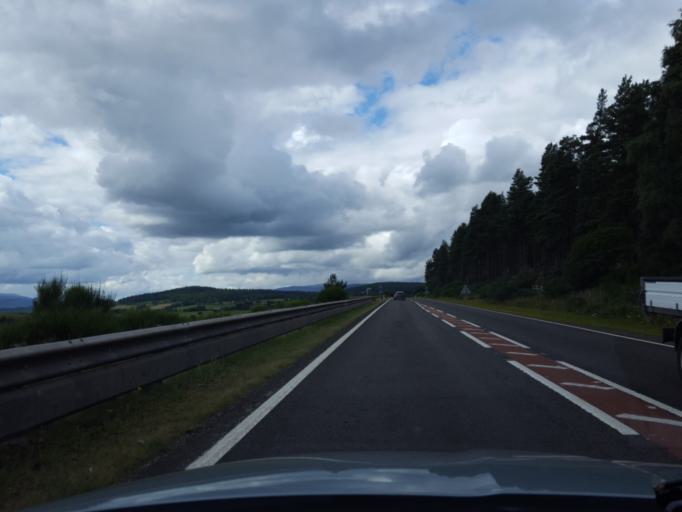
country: GB
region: Scotland
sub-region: Highland
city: Grantown on Spey
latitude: 57.3094
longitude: -3.6363
